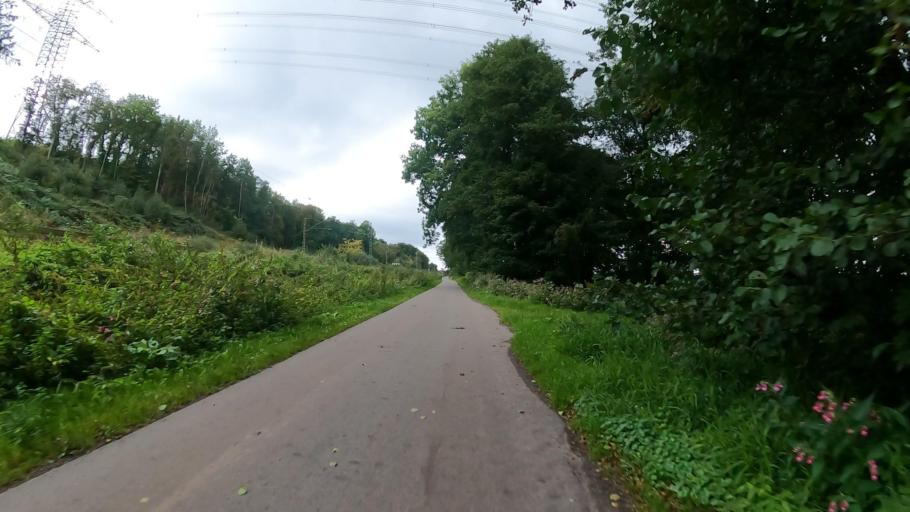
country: DE
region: Lower Saxony
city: Agathenburg
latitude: 53.5568
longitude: 9.5454
